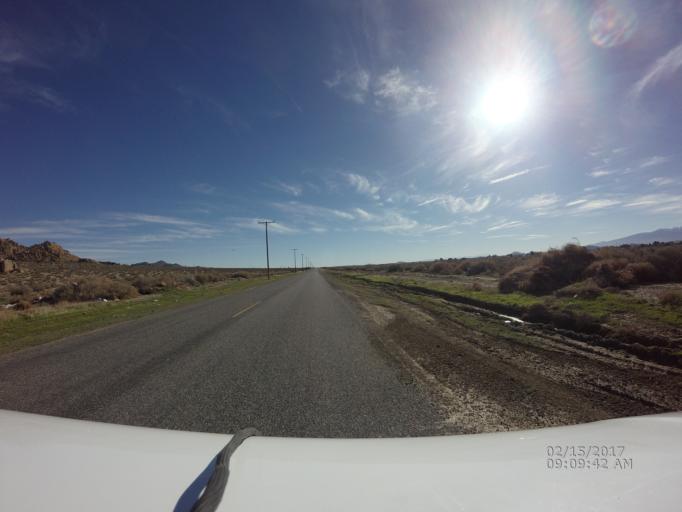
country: US
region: California
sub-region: Los Angeles County
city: Lake Los Angeles
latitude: 34.6459
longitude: -117.8568
